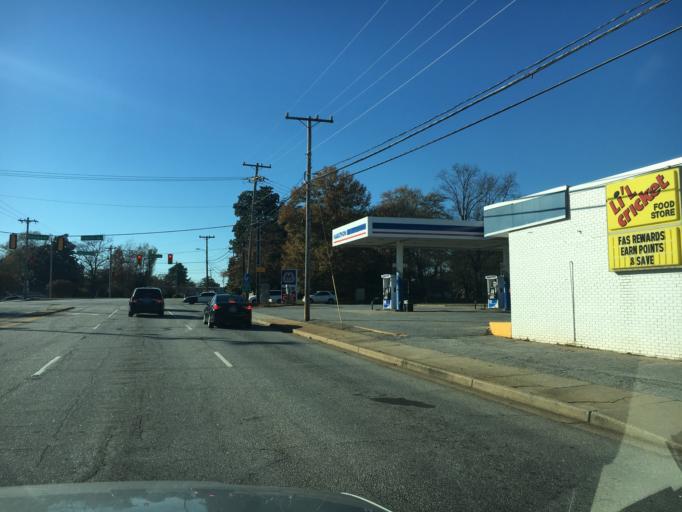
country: US
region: South Carolina
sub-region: Greenville County
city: Greer
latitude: 34.9422
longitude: -82.2473
